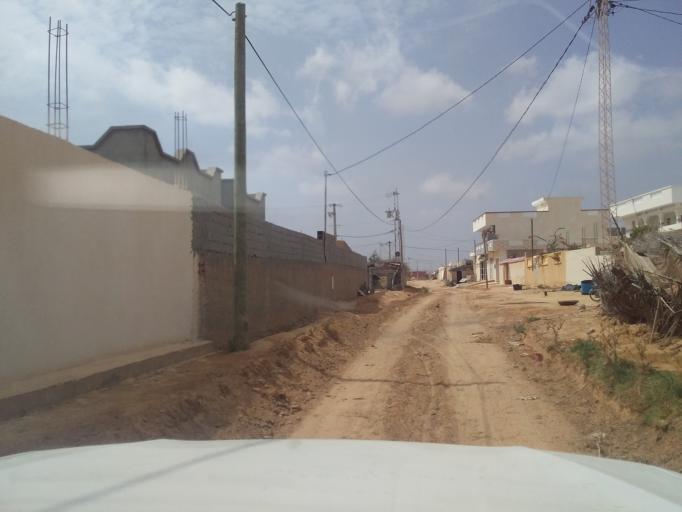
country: TN
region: Qabis
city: Matmata
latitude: 33.6203
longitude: 10.2649
